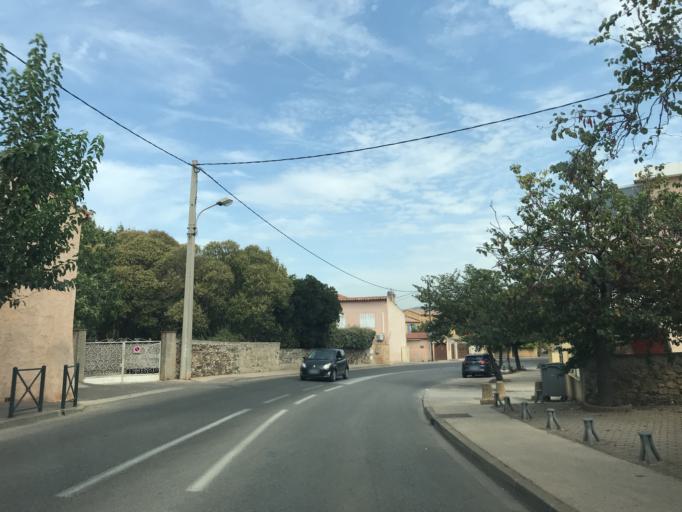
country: FR
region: Provence-Alpes-Cote d'Azur
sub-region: Departement du Var
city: Six-Fours-les-Plages
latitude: 43.0920
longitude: 5.8316
